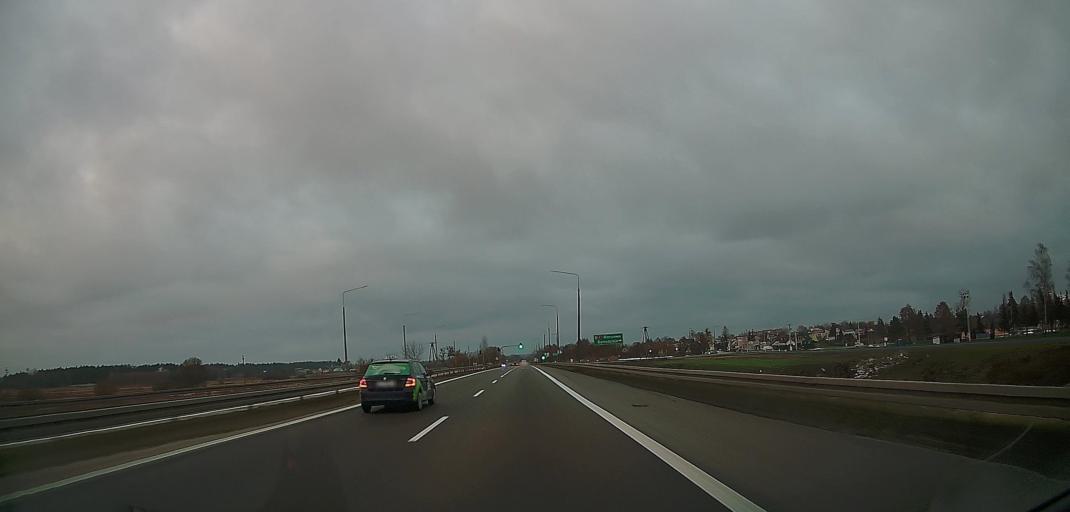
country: PL
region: Masovian Voivodeship
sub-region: Powiat radomski
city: Jedlinsk
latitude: 51.5070
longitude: 21.1181
